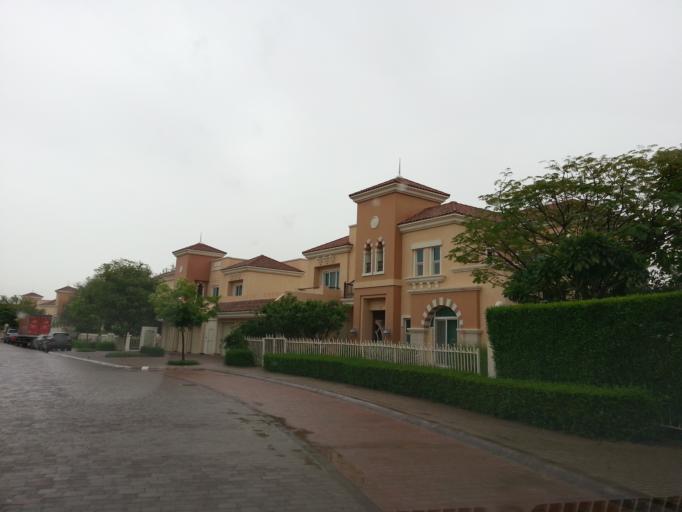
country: AE
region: Dubai
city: Dubai
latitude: 25.0325
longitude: 55.2140
